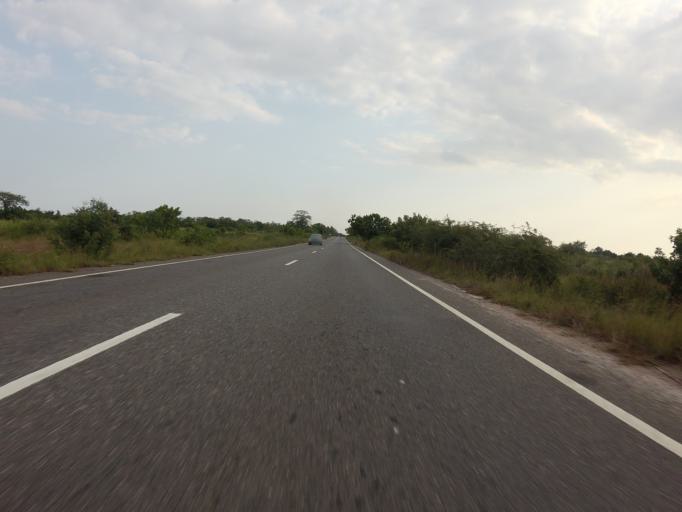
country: GH
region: Volta
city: Ho
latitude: 6.1160
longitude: 0.5186
